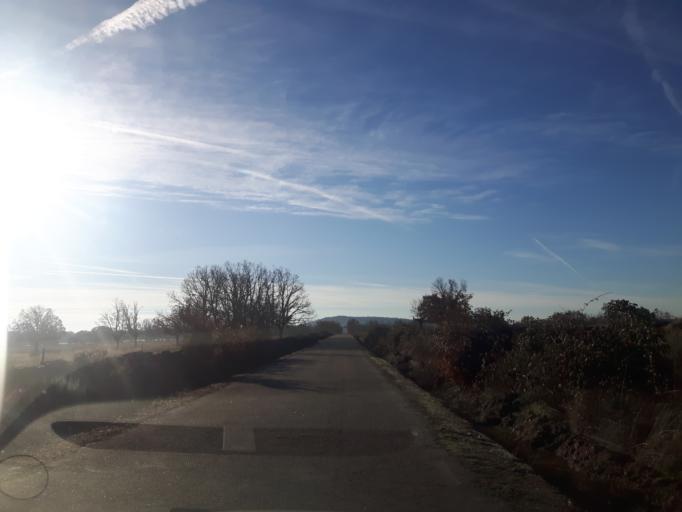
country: ES
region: Castille and Leon
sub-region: Provincia de Salamanca
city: Olmedo de Camaces
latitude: 40.9304
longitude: -6.6187
